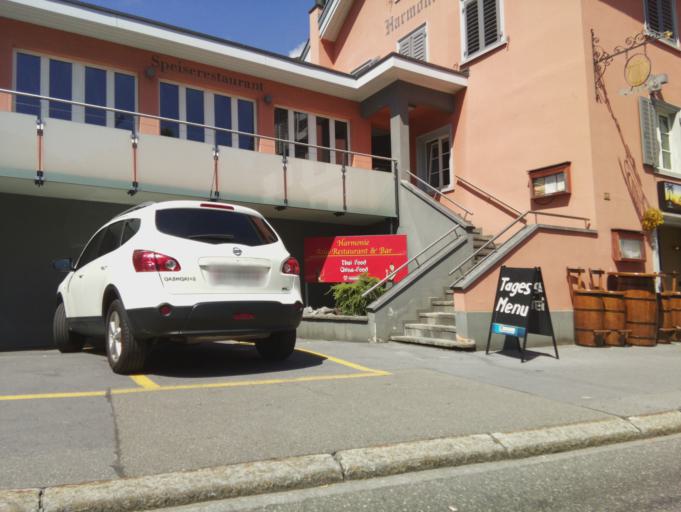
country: CH
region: Glarus
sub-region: Glarus
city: Nafels
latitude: 47.0988
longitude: 9.0633
